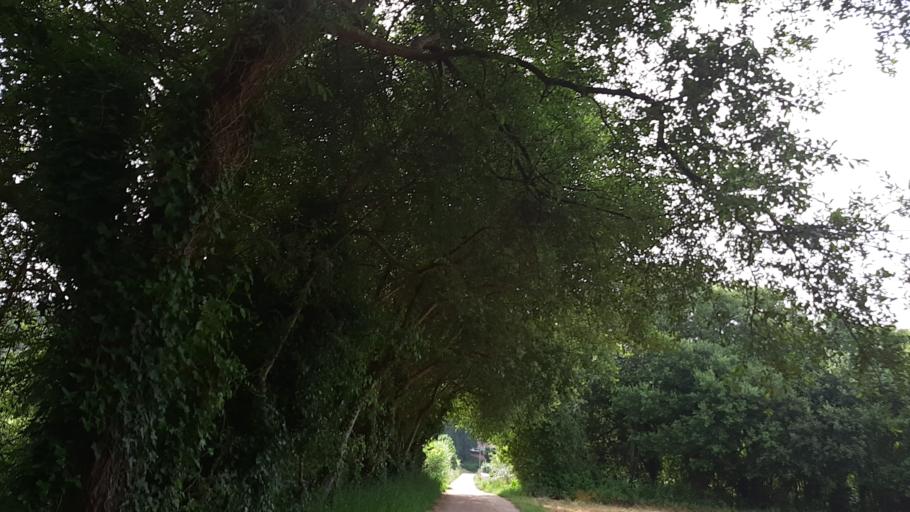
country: ES
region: Galicia
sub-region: Provincia de Pontevedra
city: O Rosal
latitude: 41.9187
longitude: -8.8286
